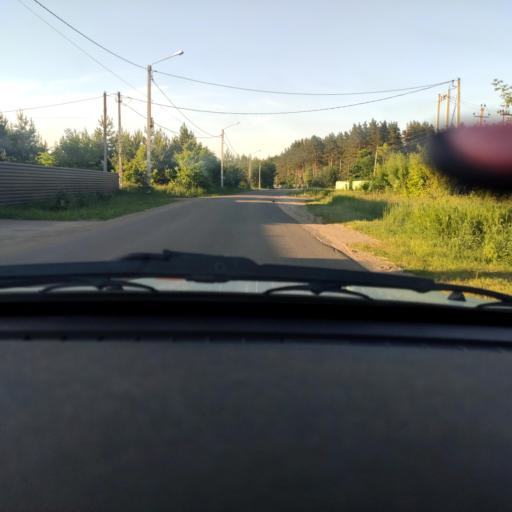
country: RU
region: Voronezj
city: Ramon'
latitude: 51.8909
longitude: 39.2721
